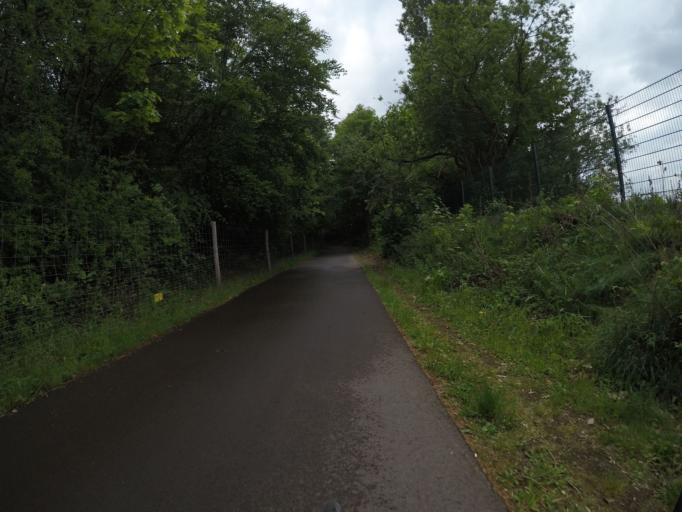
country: DE
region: Berlin
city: Lichtenberg
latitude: 52.5294
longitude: 13.5032
